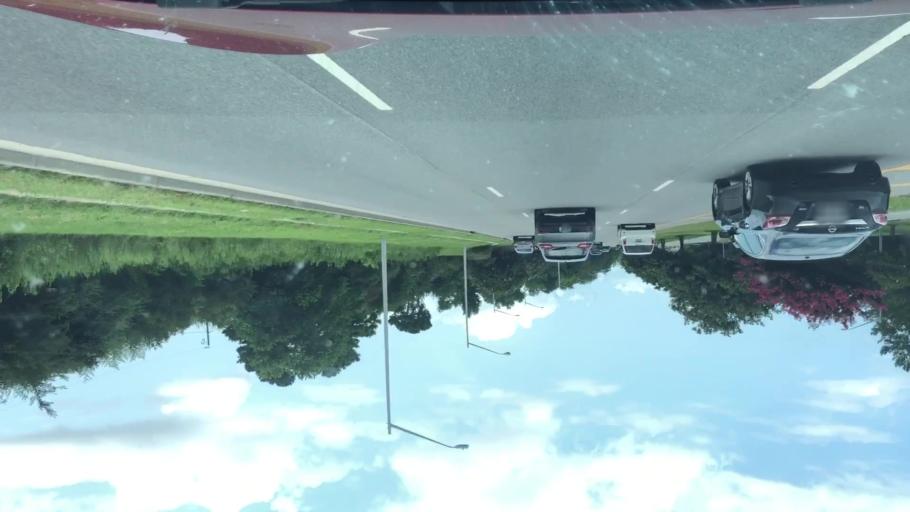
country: US
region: Virginia
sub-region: City of Chesapeake
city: Chesapeake
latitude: 36.8558
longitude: -76.1345
